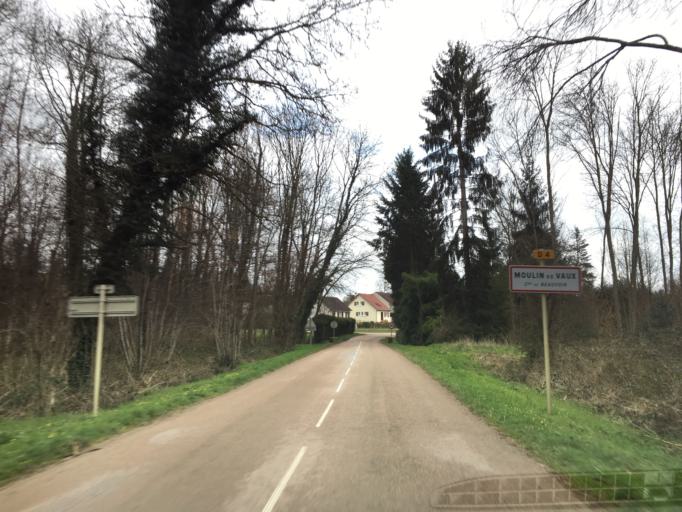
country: FR
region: Bourgogne
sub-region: Departement de l'Yonne
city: Pourrain
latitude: 47.7979
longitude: 3.3813
